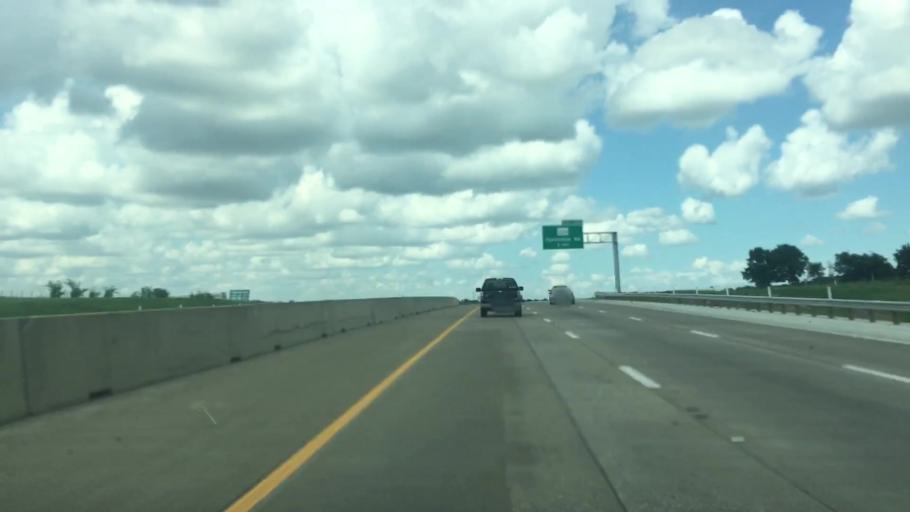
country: US
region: Texas
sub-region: Ellis County
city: Italy
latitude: 32.2406
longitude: -96.8776
